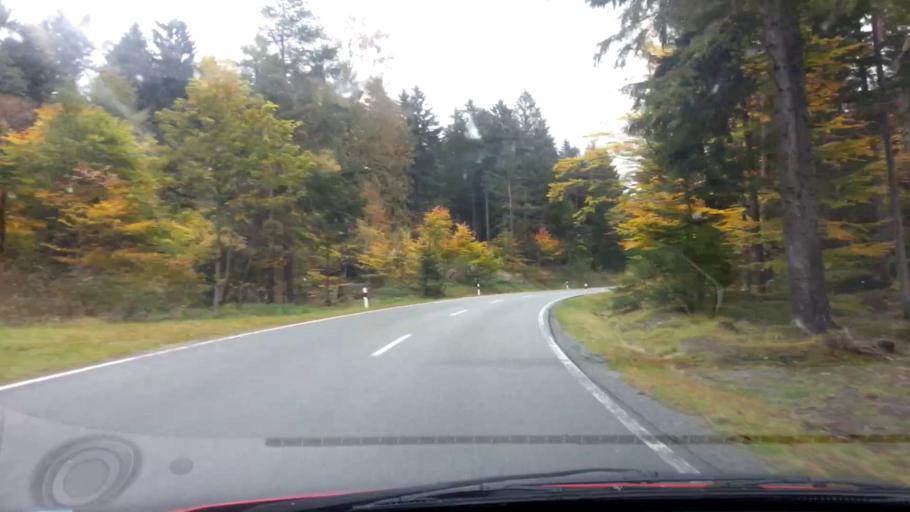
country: DE
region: Bavaria
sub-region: Upper Franconia
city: Fichtelberg
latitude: 50.0094
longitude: 11.8627
